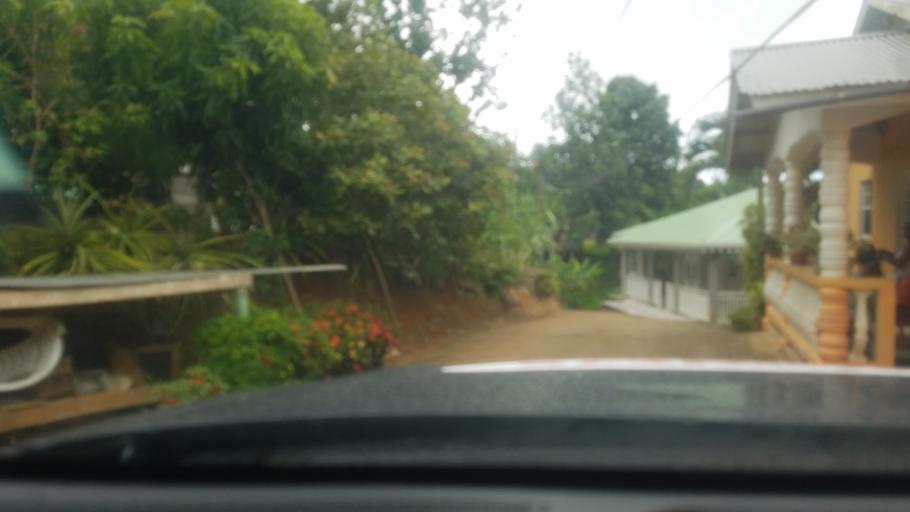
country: LC
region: Micoud Quarter
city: Micoud
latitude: 13.8047
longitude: -60.9467
